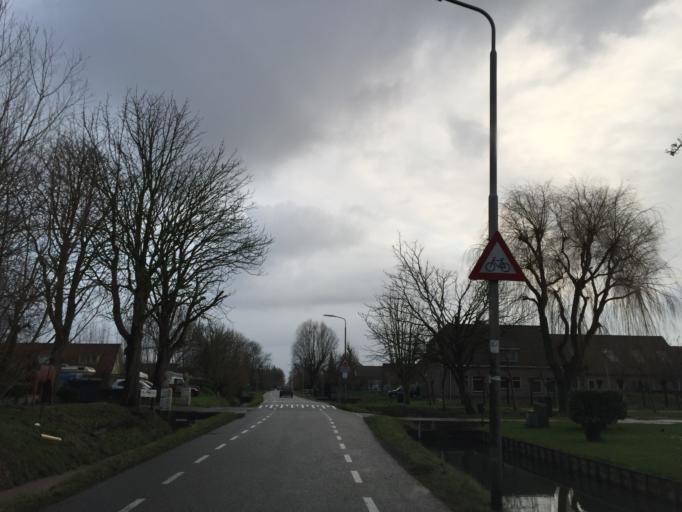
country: NL
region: South Holland
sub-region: Gemeente Pijnacker-Nootdorp
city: Pijnacker
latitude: 52.0063
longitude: 4.3980
